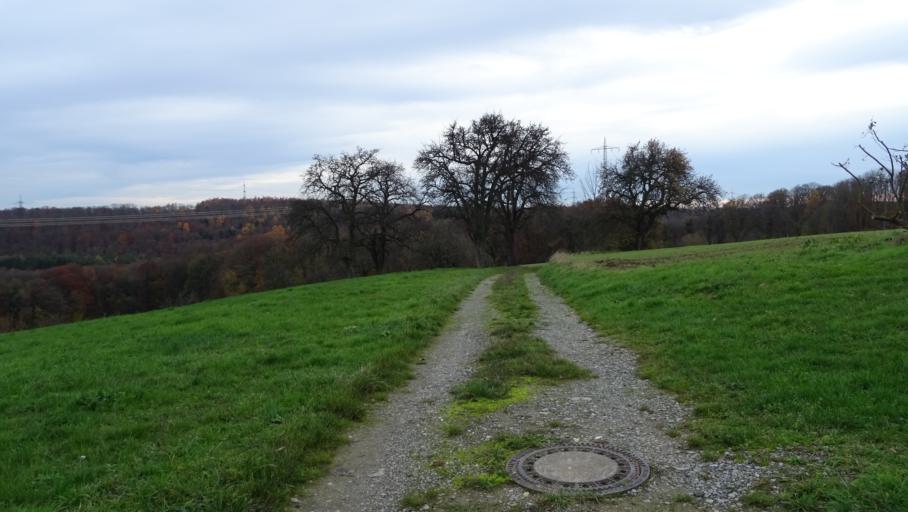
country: DE
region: Baden-Wuerttemberg
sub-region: Karlsruhe Region
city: Mosbach
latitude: 49.3415
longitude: 9.1537
